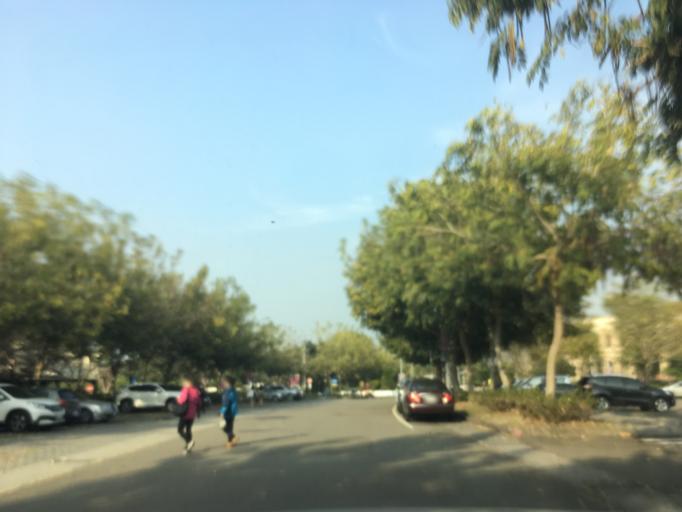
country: TW
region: Taiwan
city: Zhongxing New Village
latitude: 24.0479
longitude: 120.6859
